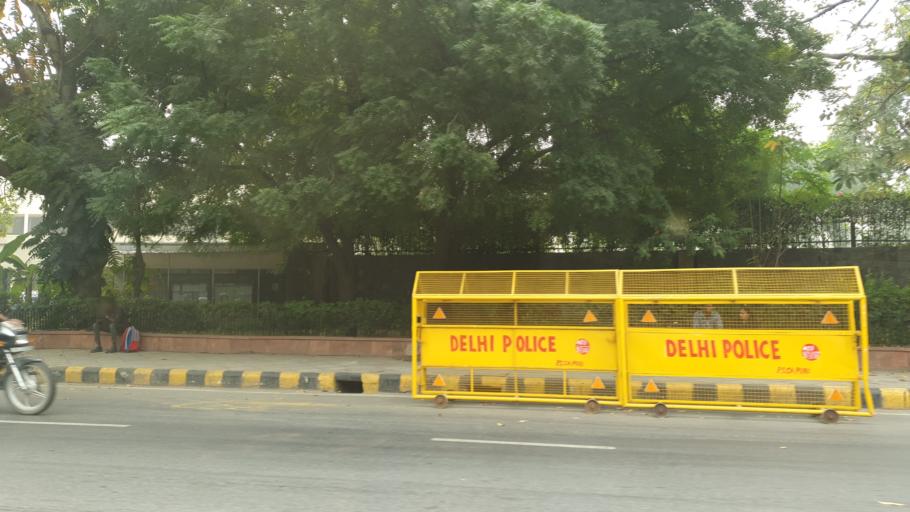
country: IN
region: NCT
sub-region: New Delhi
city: New Delhi
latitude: 28.5854
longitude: 77.1851
